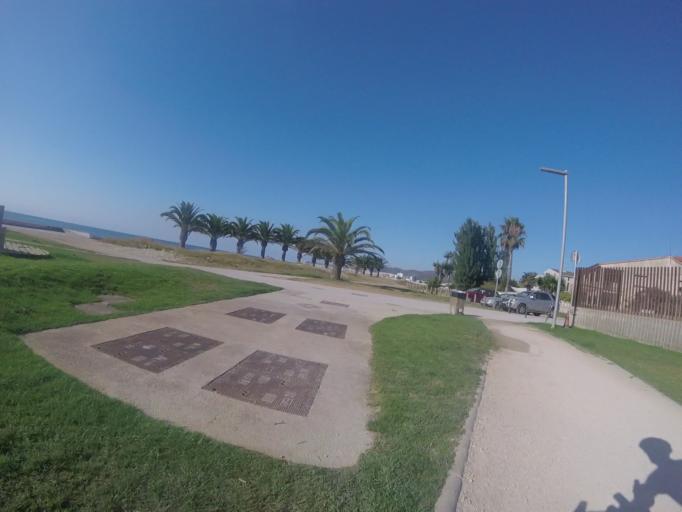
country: ES
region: Valencia
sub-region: Provincia de Castello
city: Benicarlo
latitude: 40.4100
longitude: 0.4289
